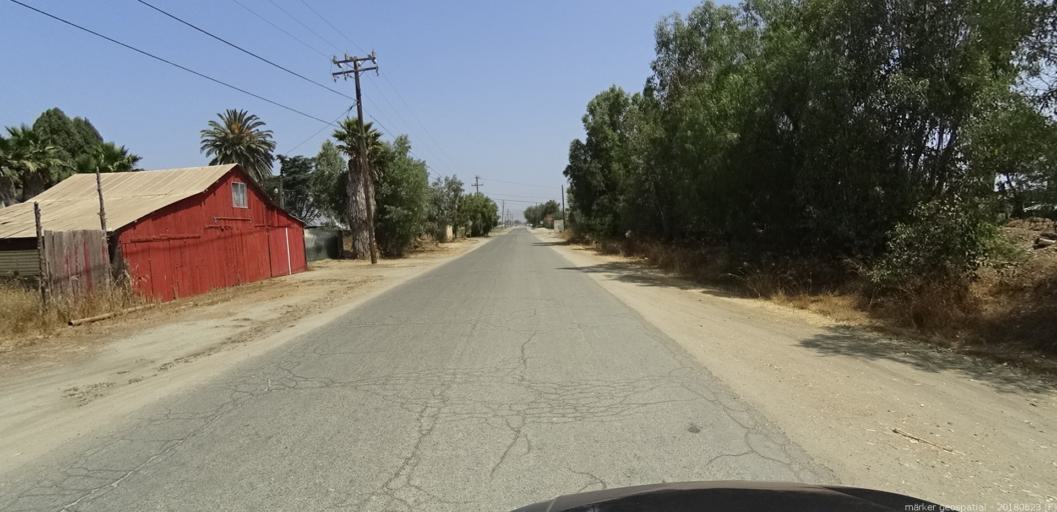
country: US
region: California
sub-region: Monterey County
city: Greenfield
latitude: 36.3151
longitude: -121.2616
